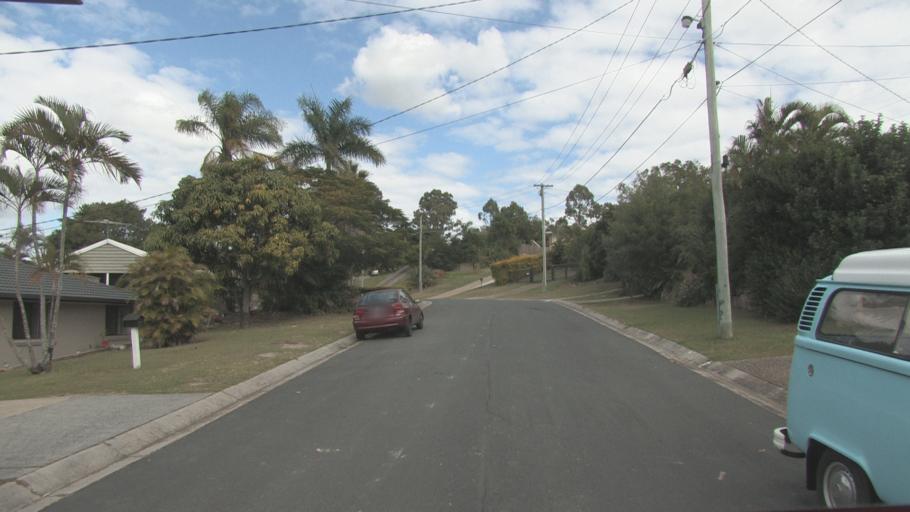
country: AU
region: Queensland
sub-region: Logan
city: Windaroo
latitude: -27.7295
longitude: 153.2050
